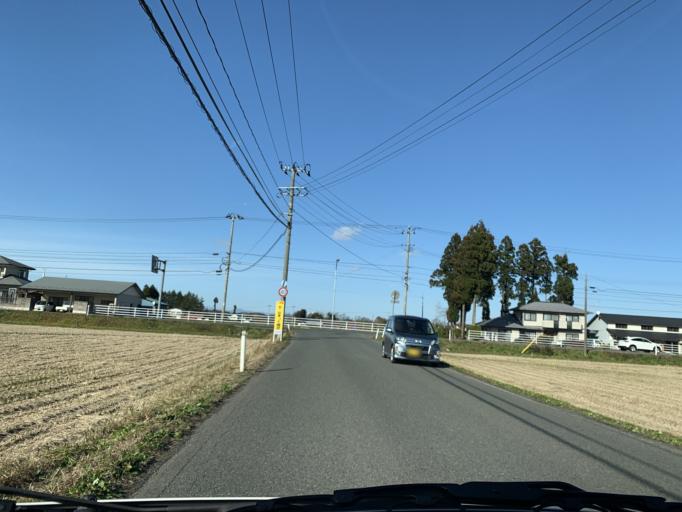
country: JP
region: Iwate
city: Mizusawa
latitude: 39.1633
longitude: 141.0989
